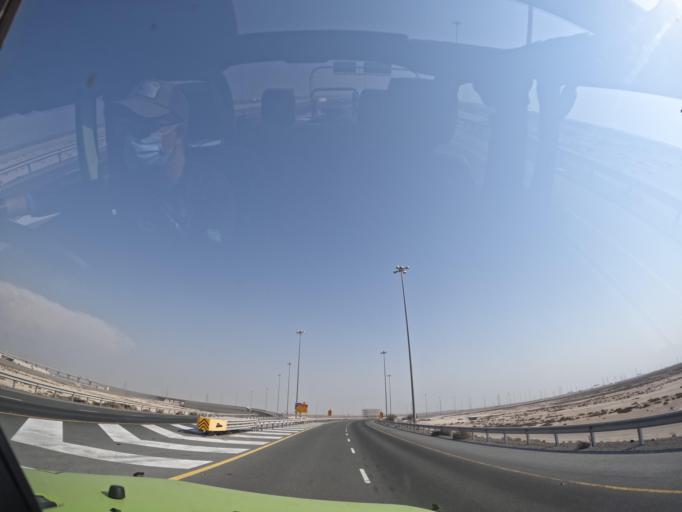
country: AE
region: Abu Dhabi
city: Abu Dhabi
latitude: 24.6793
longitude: 54.8103
